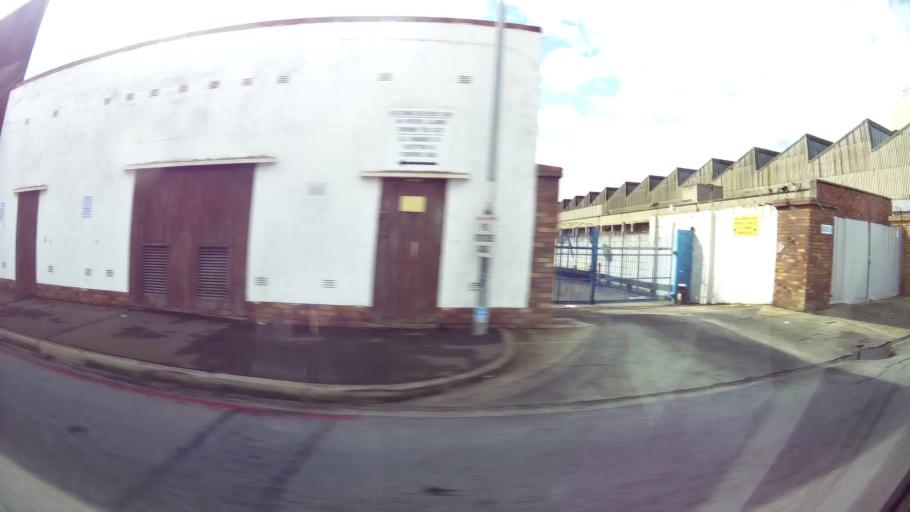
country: ZA
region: Eastern Cape
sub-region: Nelson Mandela Bay Metropolitan Municipality
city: Port Elizabeth
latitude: -33.9311
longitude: 25.5790
